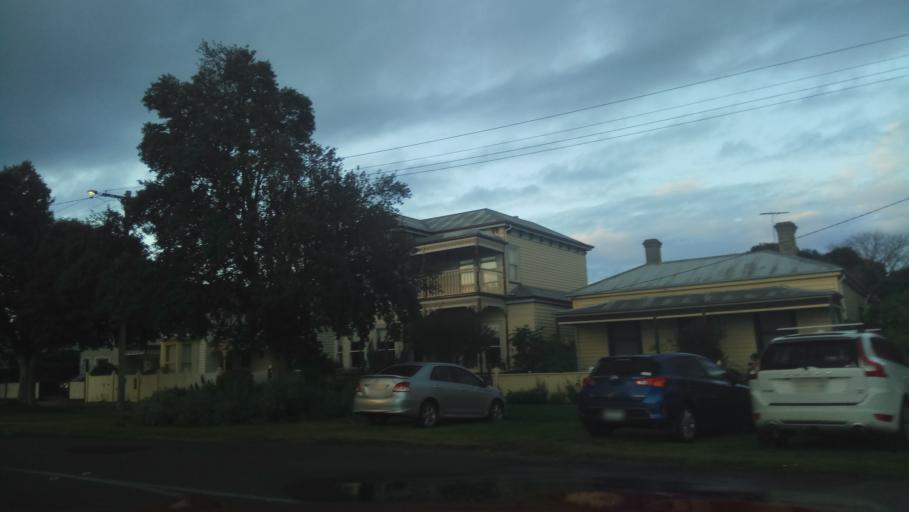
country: AU
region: Victoria
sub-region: Hobsons Bay
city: Williamstown
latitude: -37.8699
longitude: 144.9039
